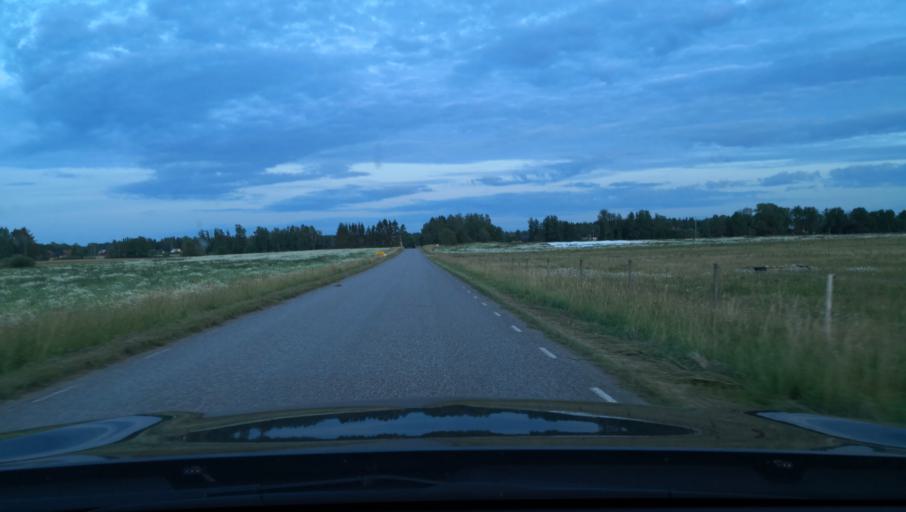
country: SE
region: Uppsala
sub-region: Osthammars Kommun
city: Bjorklinge
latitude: 60.0456
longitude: 17.4976
